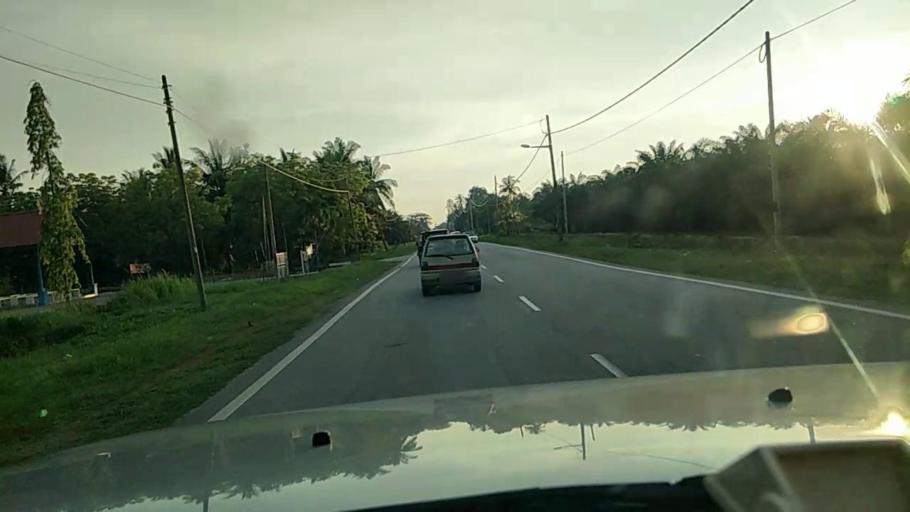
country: MY
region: Selangor
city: Kuala Selangor
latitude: 3.3047
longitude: 101.3020
